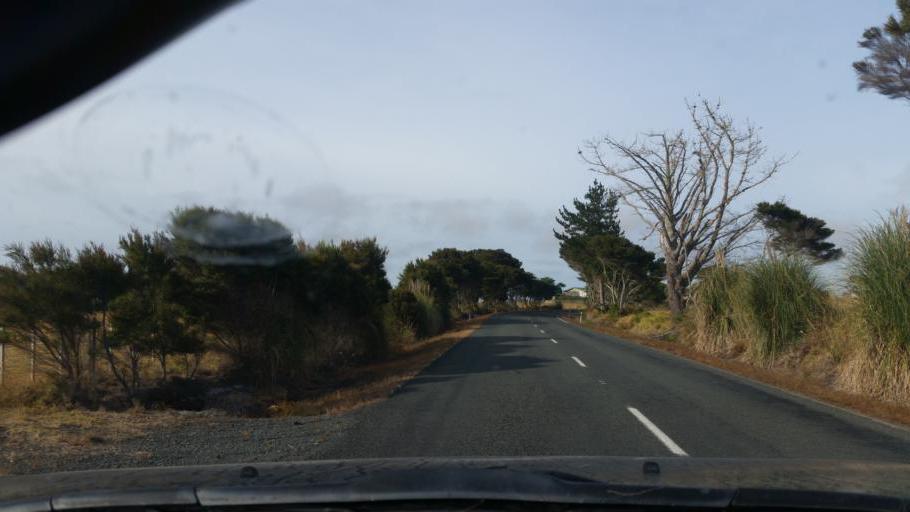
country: NZ
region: Northland
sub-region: Kaipara District
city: Dargaville
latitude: -36.1982
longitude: 174.0506
